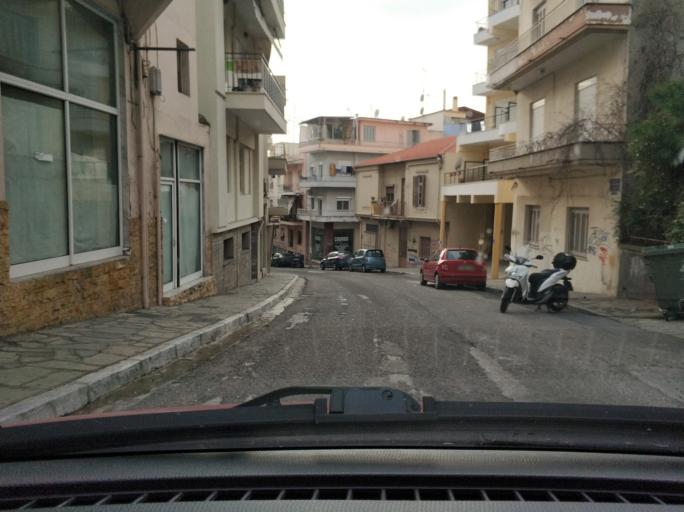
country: GR
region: East Macedonia and Thrace
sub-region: Nomos Kavalas
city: Kavala
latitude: 40.9404
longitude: 24.4170
